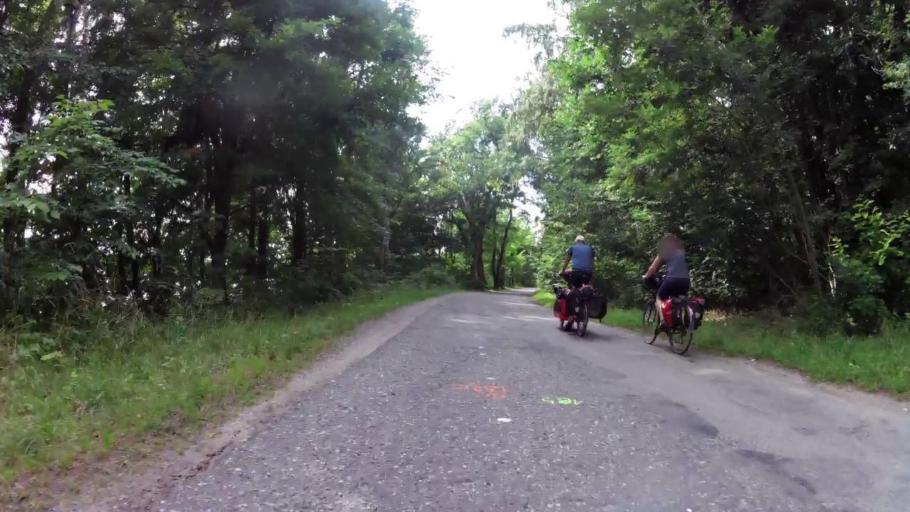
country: PL
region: West Pomeranian Voivodeship
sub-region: Powiat lobeski
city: Wegorzyno
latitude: 53.5417
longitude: 15.5793
